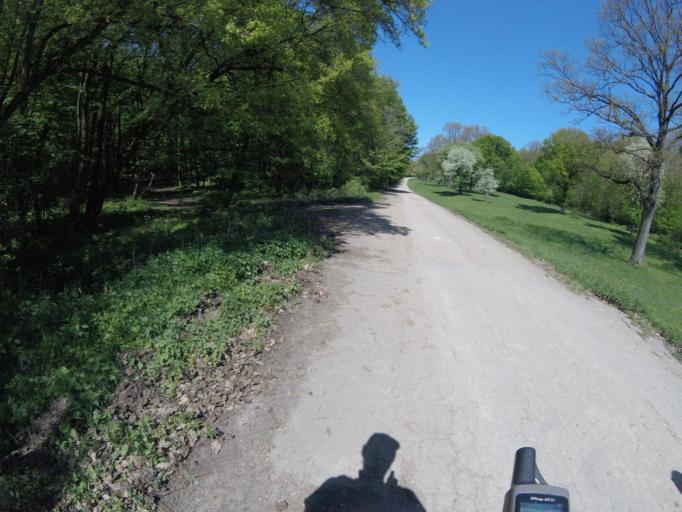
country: HU
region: Pest
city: Nagymaros
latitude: 47.8049
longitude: 18.9418
